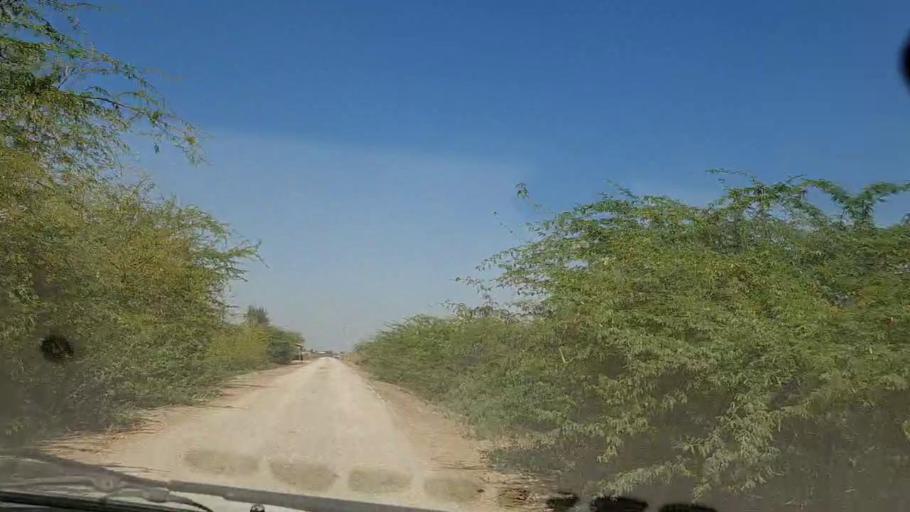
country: PK
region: Sindh
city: Mirpur Khas
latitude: 25.4274
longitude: 69.0439
